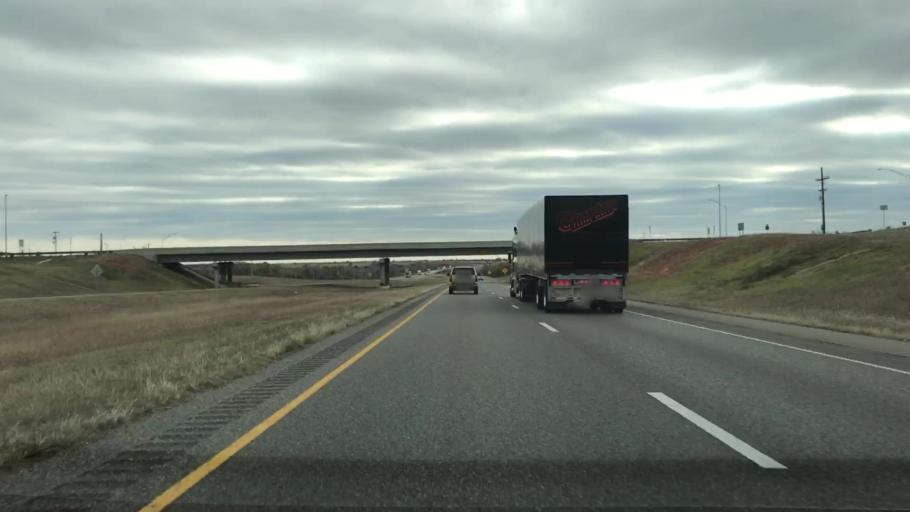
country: US
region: Oklahoma
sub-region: Beckham County
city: Sayre
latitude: 35.2932
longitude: -99.6199
